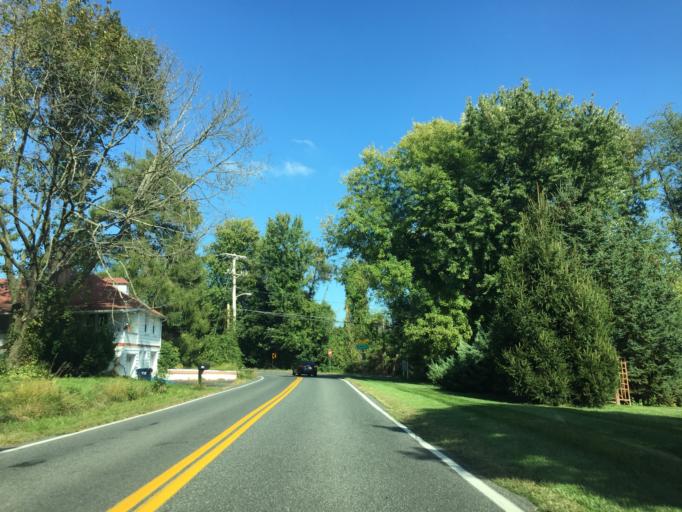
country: US
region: Maryland
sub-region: Harford County
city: Fallston
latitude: 39.5579
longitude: -76.4226
